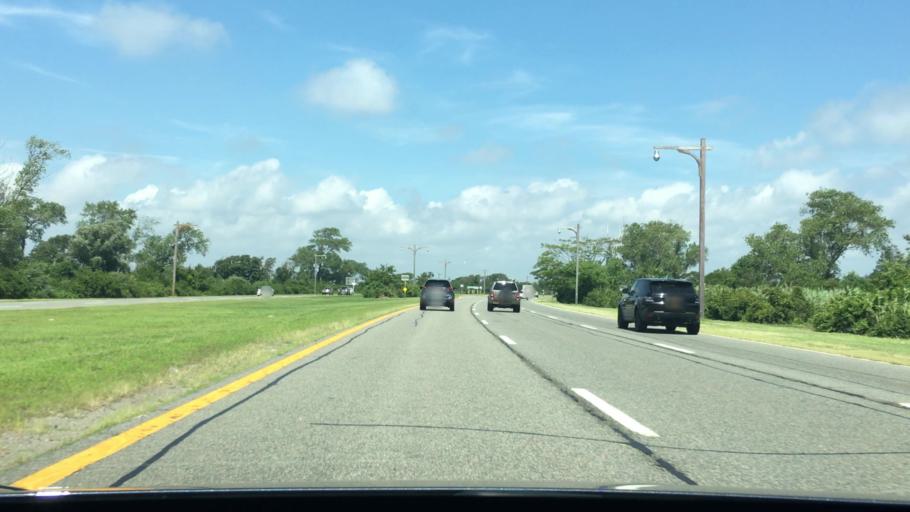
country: US
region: New York
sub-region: Nassau County
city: Point Lookout
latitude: 40.6187
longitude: -73.5585
